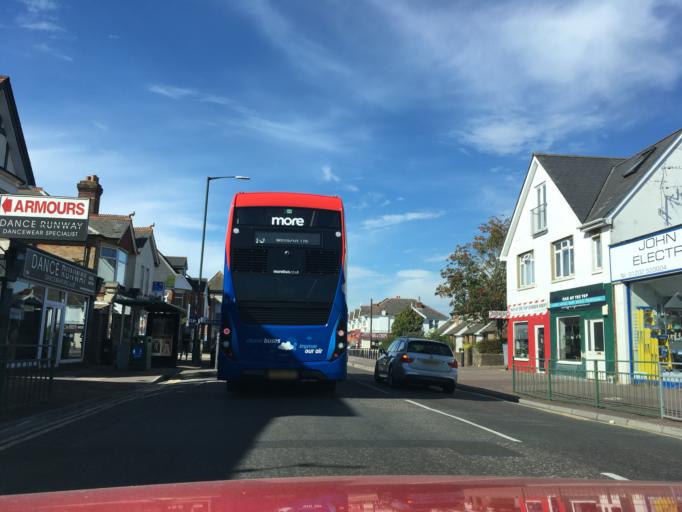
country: GB
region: England
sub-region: Bournemouth
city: Bournemouth
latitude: 50.7509
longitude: -1.8770
